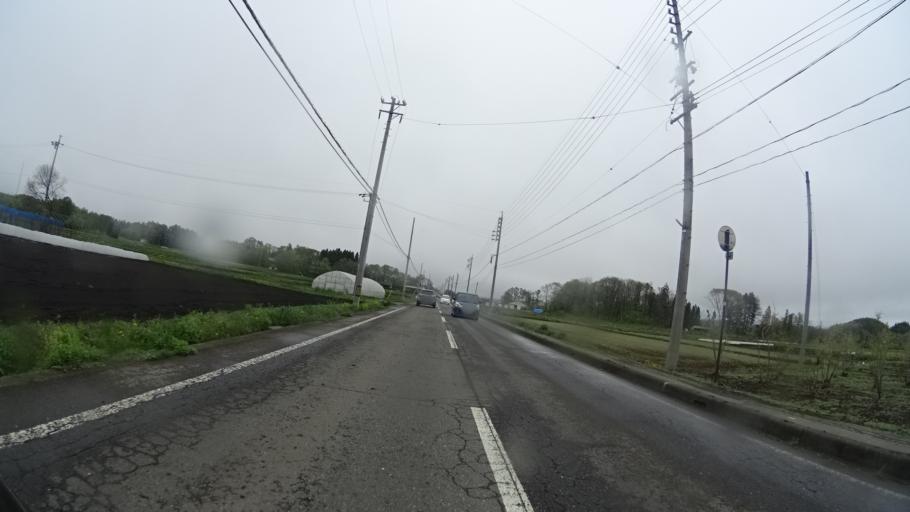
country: JP
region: Nagano
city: Nagano-shi
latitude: 36.7814
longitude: 138.1999
